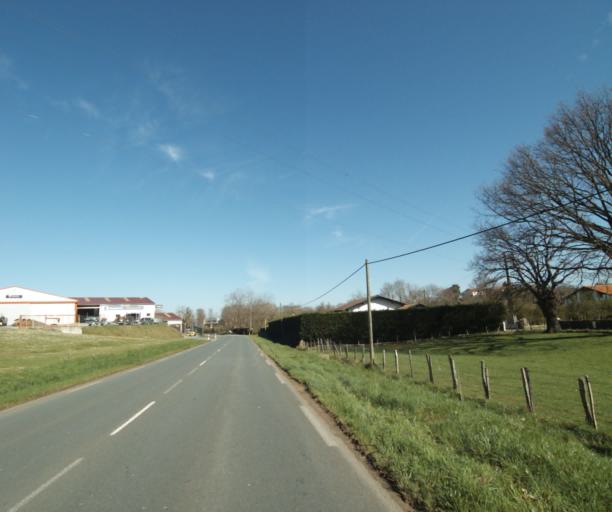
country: FR
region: Aquitaine
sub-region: Departement des Pyrenees-Atlantiques
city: Urrugne
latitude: 43.3439
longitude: -1.6901
